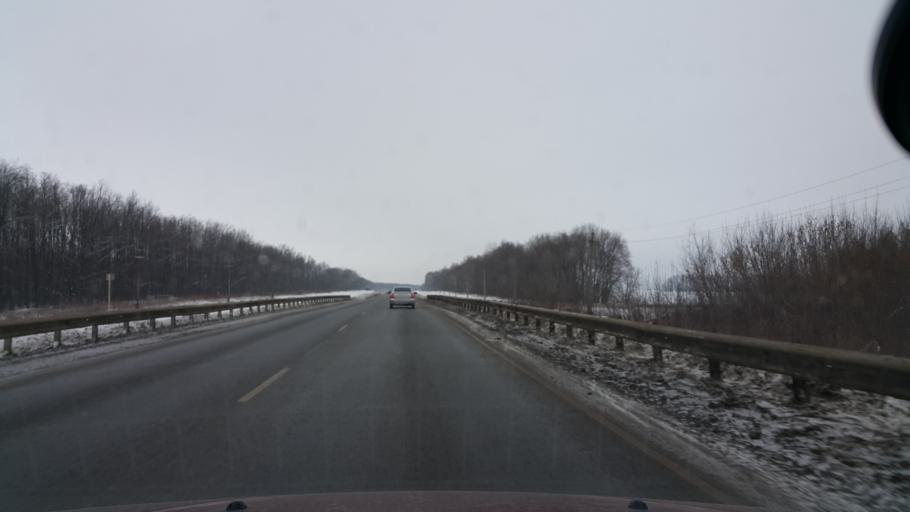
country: RU
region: Tambov
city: Kotovsk
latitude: 52.5825
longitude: 41.4509
